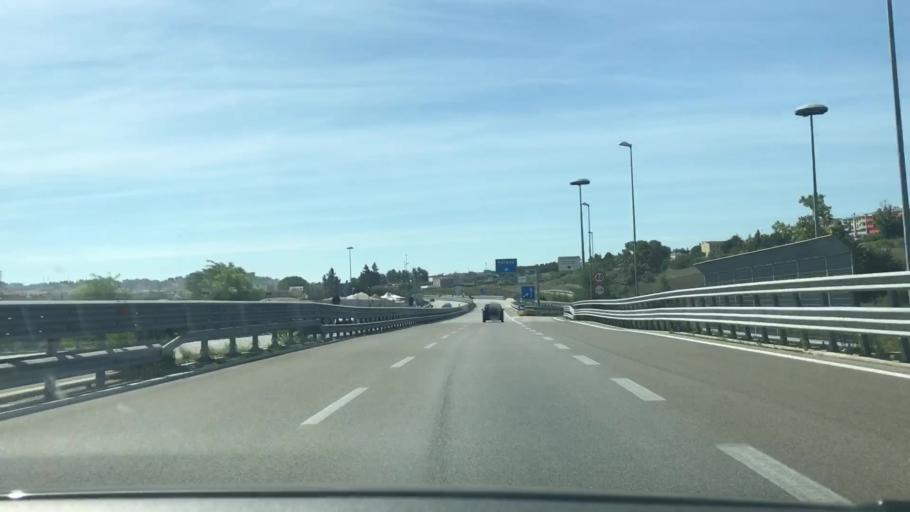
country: IT
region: Basilicate
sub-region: Provincia di Matera
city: Matera
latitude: 40.6916
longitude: 16.5912
